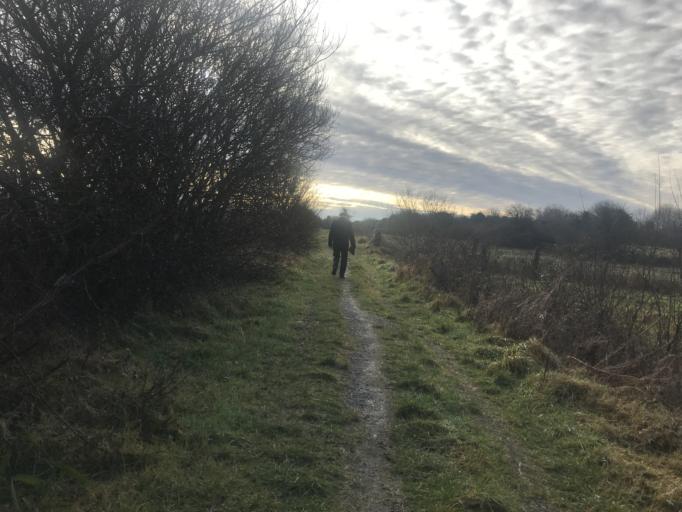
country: IE
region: Connaught
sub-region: County Galway
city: Claregalway
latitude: 53.3173
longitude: -9.0046
